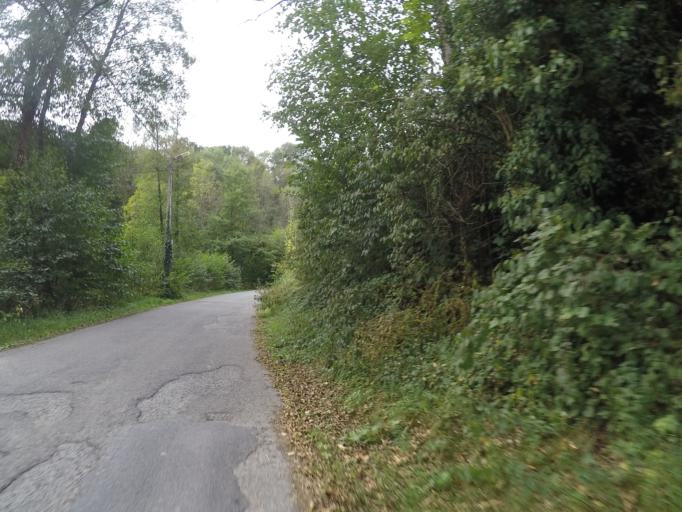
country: BE
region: Wallonia
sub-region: Province de Namur
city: Dinant
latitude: 50.2731
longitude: 4.9549
